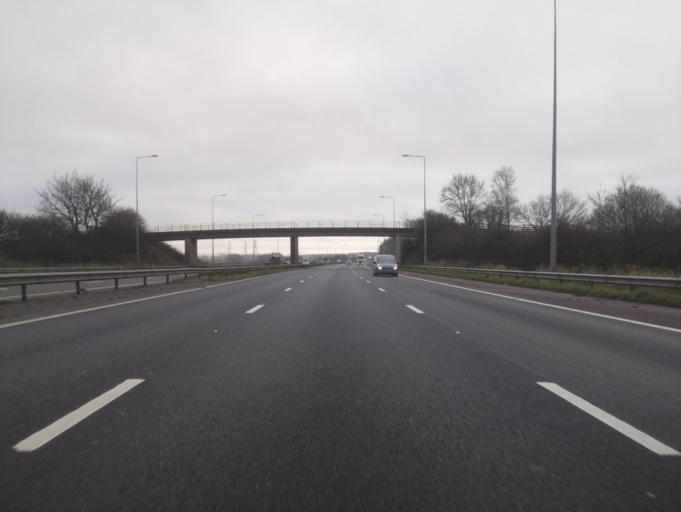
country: GB
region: England
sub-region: Lancashire
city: Coppull
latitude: 53.6214
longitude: -2.6864
